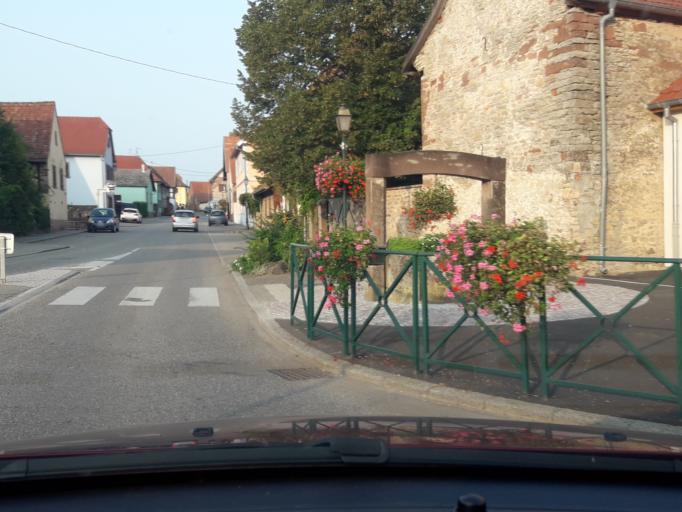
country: FR
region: Alsace
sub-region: Departement du Bas-Rhin
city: Wasselonne
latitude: 48.6617
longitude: 7.4736
